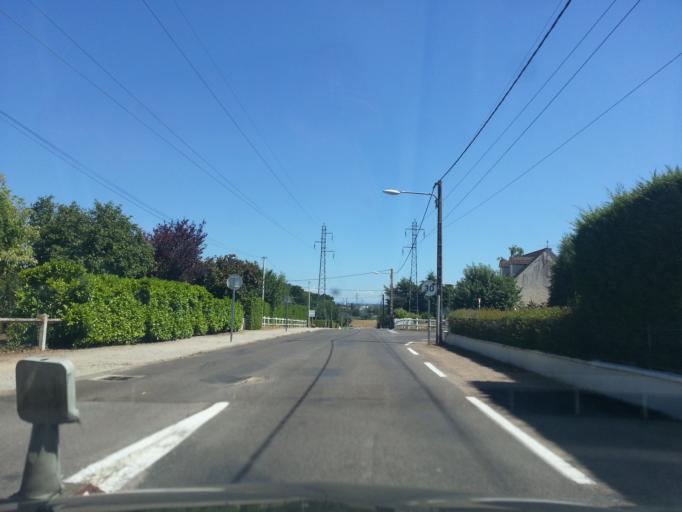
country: FR
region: Bourgogne
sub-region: Departement de Saone-et-Loire
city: Chatenoy-le-Royal
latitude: 46.7869
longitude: 4.8113
